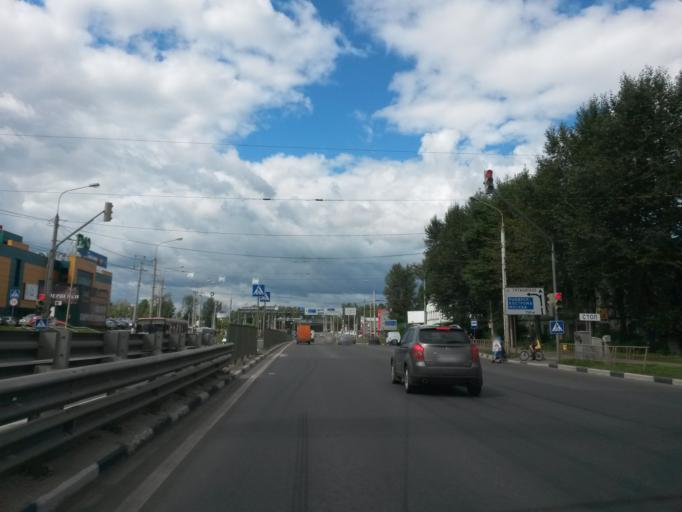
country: RU
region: Jaroslavl
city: Yaroslavl
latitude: 57.6703
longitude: 39.8399
